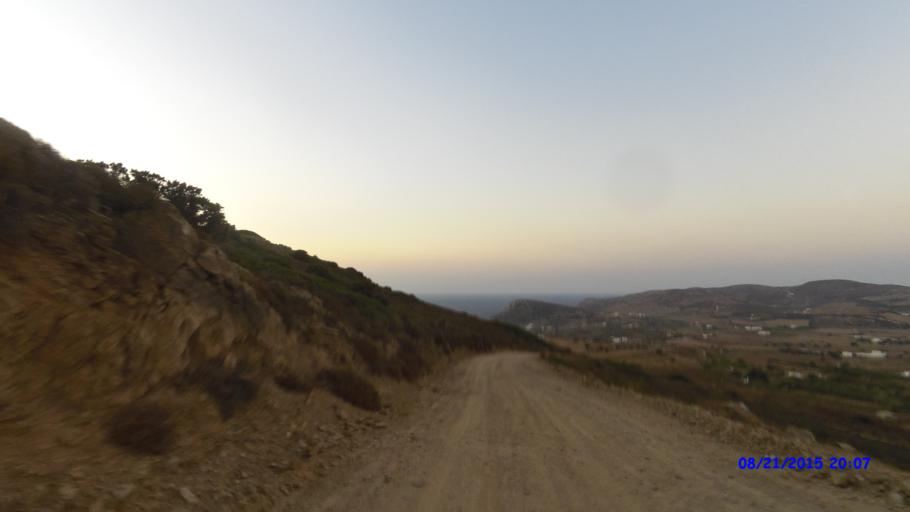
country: GR
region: South Aegean
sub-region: Nomos Kykladon
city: Antiparos
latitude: 37.0082
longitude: 25.0458
